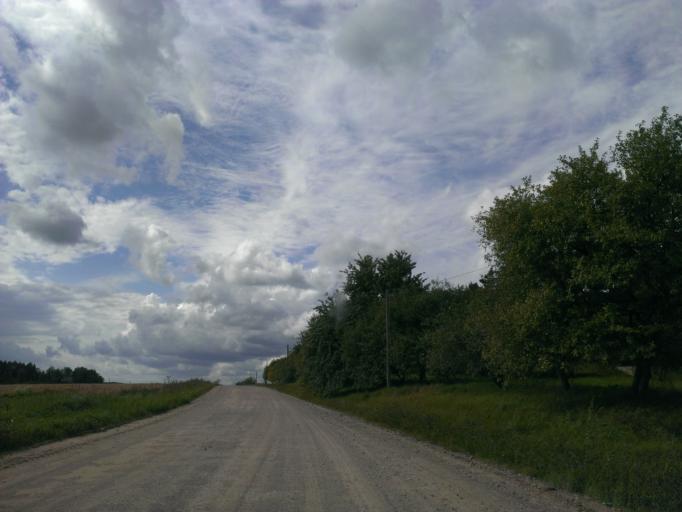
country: LV
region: Skriveri
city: Skriveri
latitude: 56.8378
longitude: 25.2095
